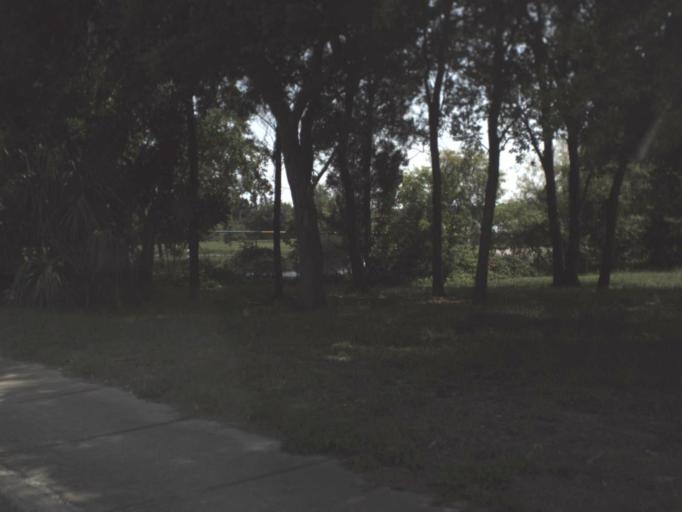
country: US
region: Florida
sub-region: Pinellas County
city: Seminole
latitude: 27.8522
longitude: -82.7870
